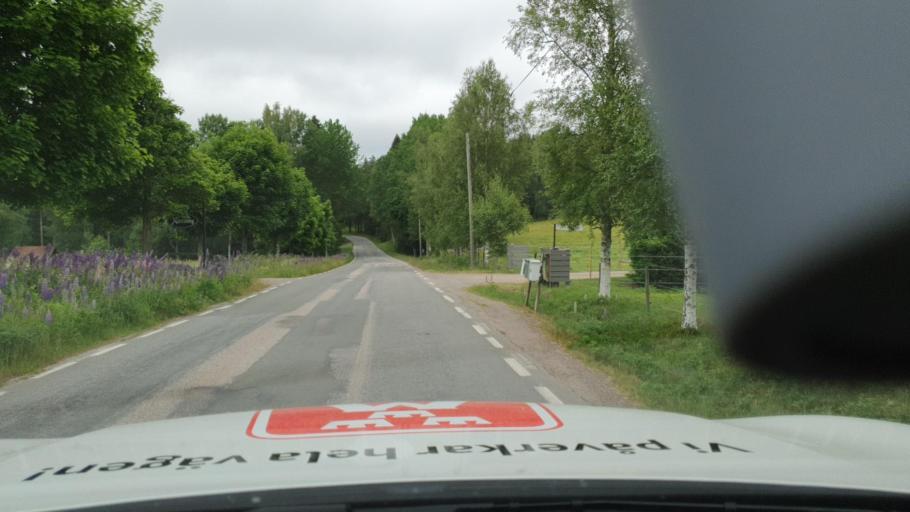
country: SE
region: Vaestra Goetaland
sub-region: Tibro Kommun
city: Tibro
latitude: 58.3712
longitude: 14.2013
